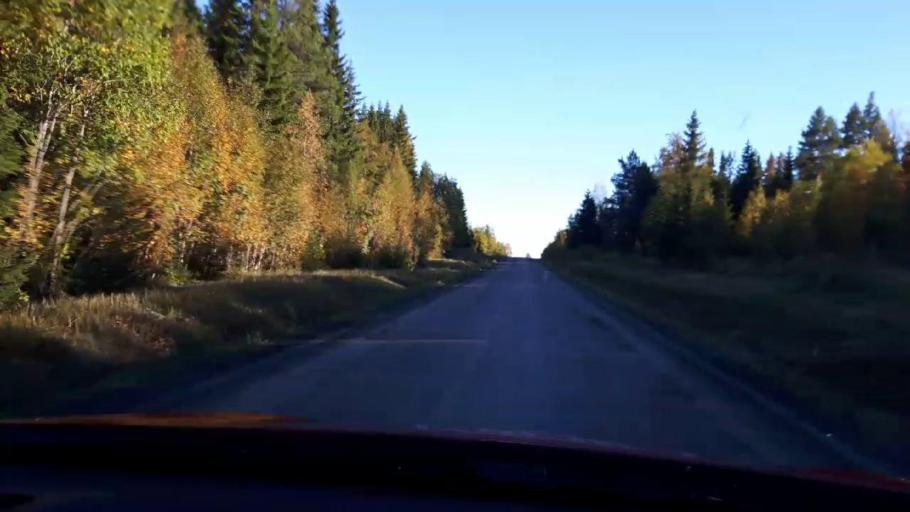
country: SE
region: Jaemtland
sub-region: OEstersunds Kommun
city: Lit
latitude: 63.6639
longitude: 14.7132
